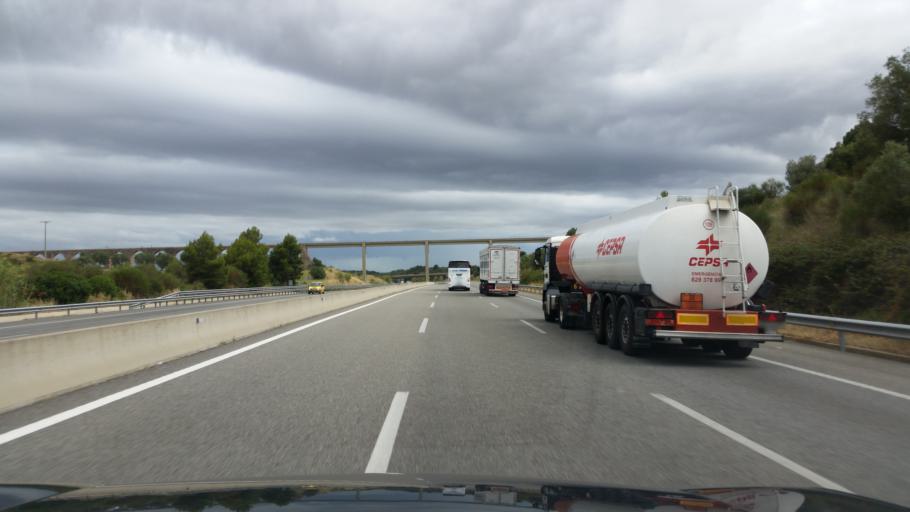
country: ES
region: Catalonia
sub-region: Provincia de Girona
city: Figueres
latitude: 42.2787
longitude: 2.9409
